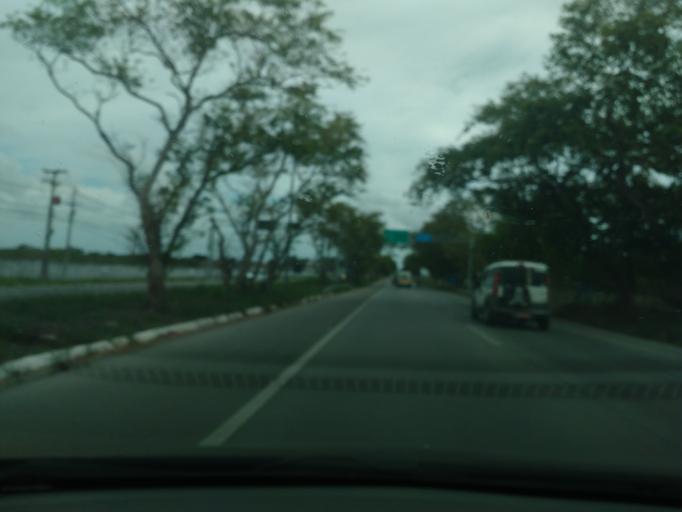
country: BR
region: Alagoas
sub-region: Satuba
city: Satuba
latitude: -9.5198
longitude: -35.8025
